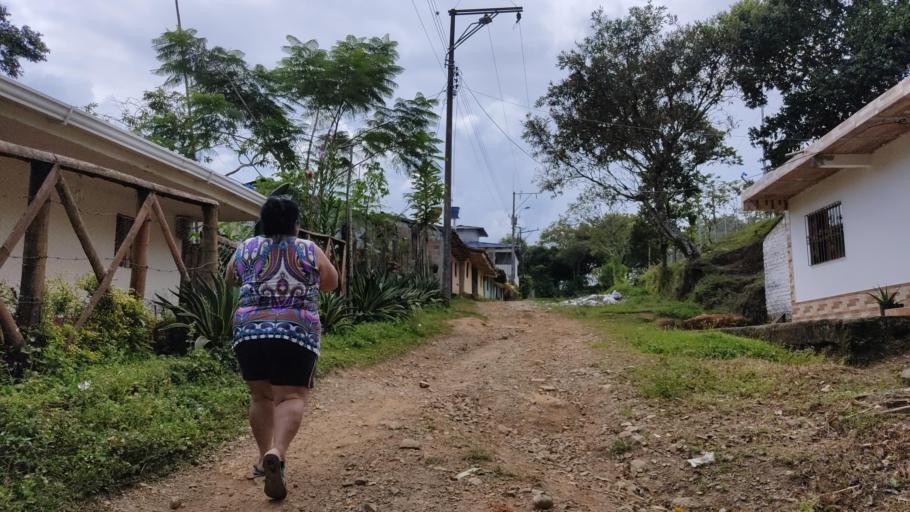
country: CO
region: Valle del Cauca
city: Jamundi
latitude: 3.2105
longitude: -76.6554
